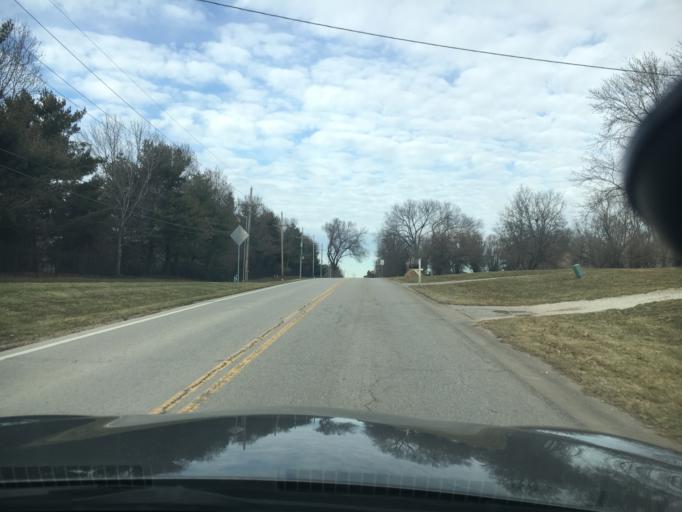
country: US
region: Missouri
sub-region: Jackson County
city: Grandview
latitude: 38.8557
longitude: -94.6305
